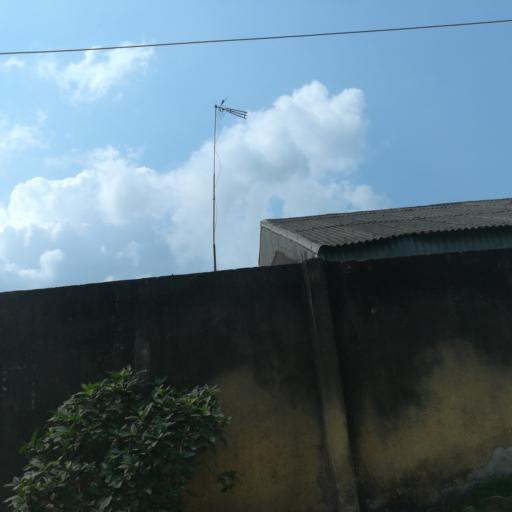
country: NG
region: Rivers
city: Okrika
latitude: 4.7900
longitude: 7.1189
